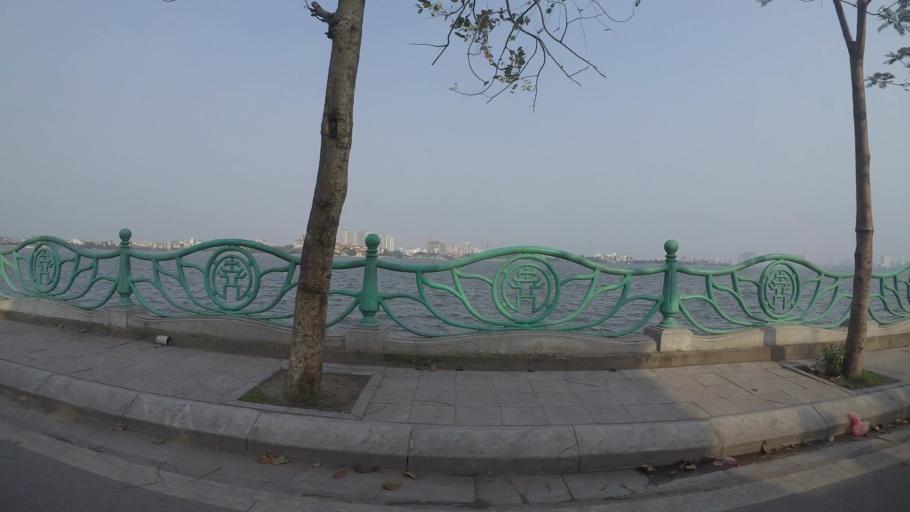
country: VN
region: Ha Noi
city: Tay Ho
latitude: 21.0682
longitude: 105.8122
